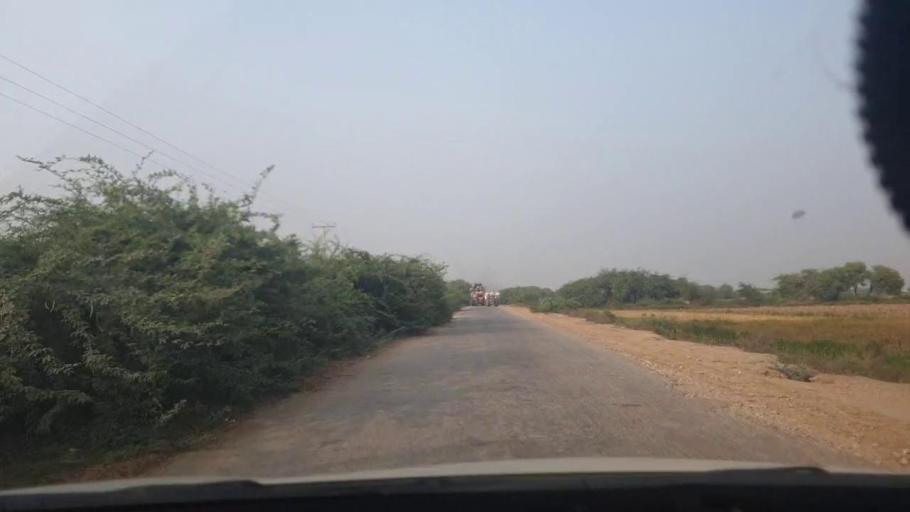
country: PK
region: Sindh
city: Bulri
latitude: 24.7662
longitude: 68.4205
